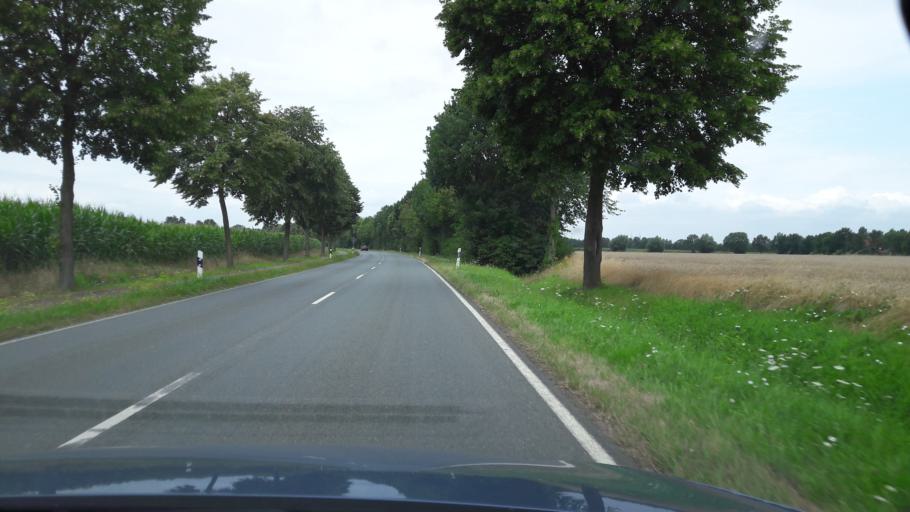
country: DE
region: North Rhine-Westphalia
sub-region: Regierungsbezirk Munster
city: Warendorf
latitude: 51.8665
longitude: 7.9354
